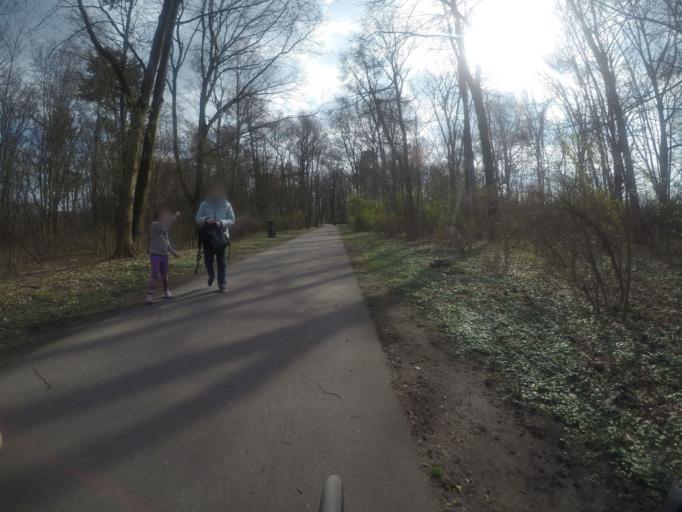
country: DE
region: Berlin
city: Britz
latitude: 52.4441
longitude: 13.4396
